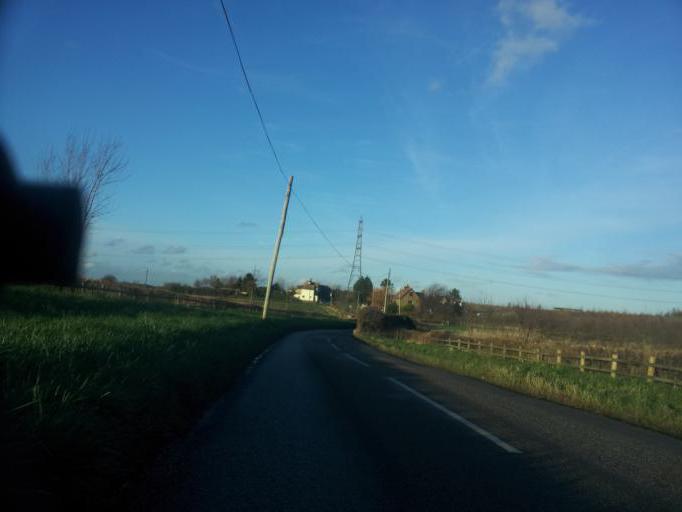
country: GB
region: England
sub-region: Kent
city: Meopham
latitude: 51.3990
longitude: 0.3861
